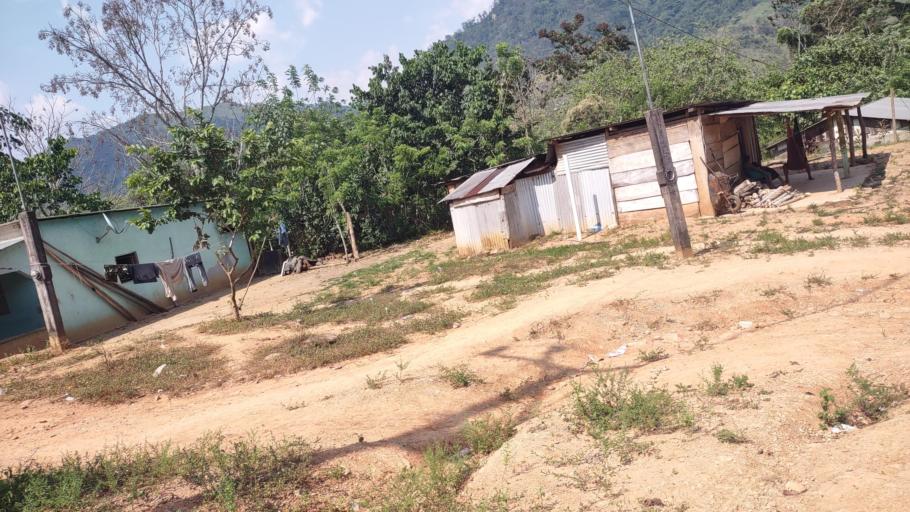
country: MX
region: Chiapas
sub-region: Tecpatan
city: Raudales Malpaso
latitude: 17.3461
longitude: -93.7603
